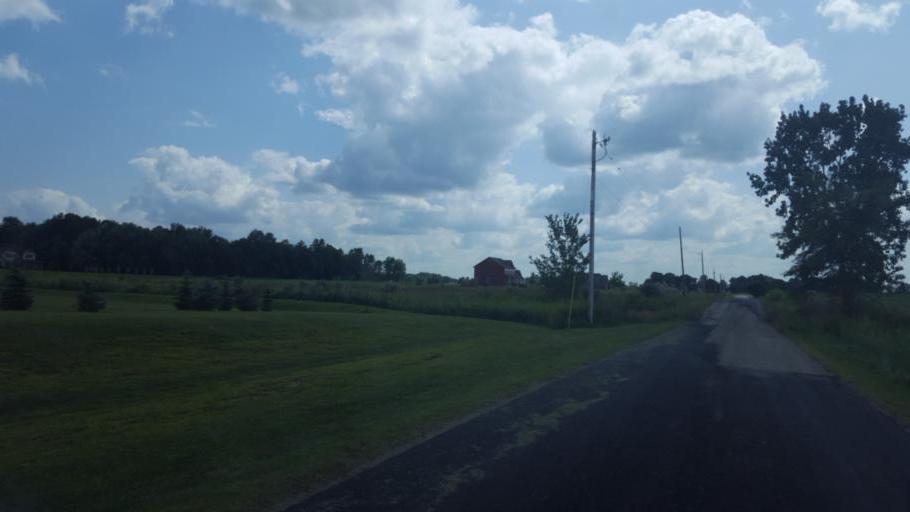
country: US
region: Ohio
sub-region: Delaware County
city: Sunbury
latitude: 40.3541
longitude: -82.8560
